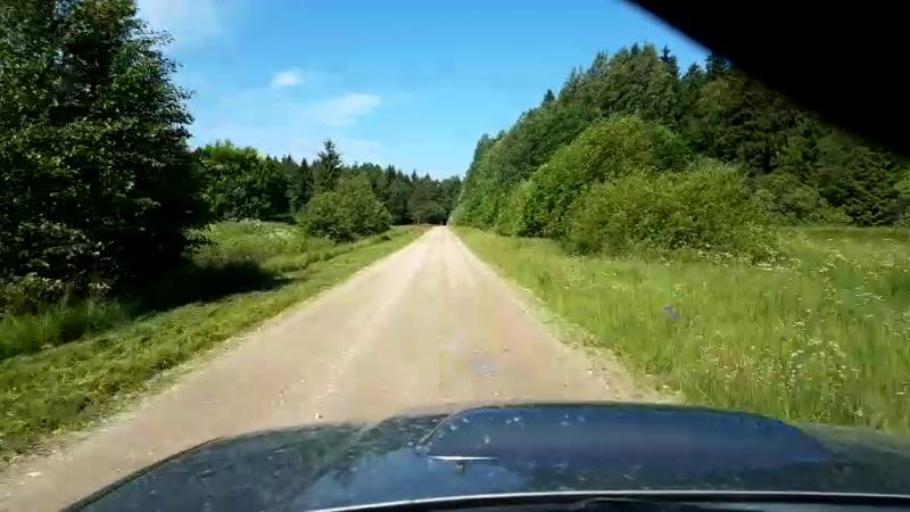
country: EE
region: Paernumaa
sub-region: Sindi linn
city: Sindi
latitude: 58.5180
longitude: 24.6513
